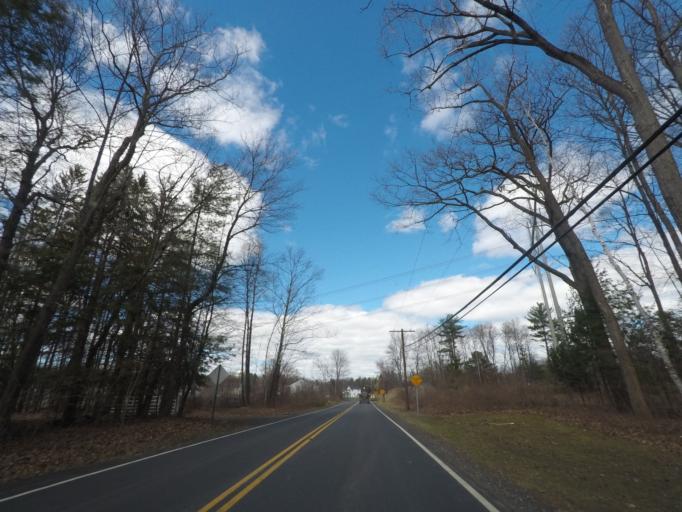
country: US
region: New York
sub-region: Albany County
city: Delmar
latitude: 42.5792
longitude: -73.8295
